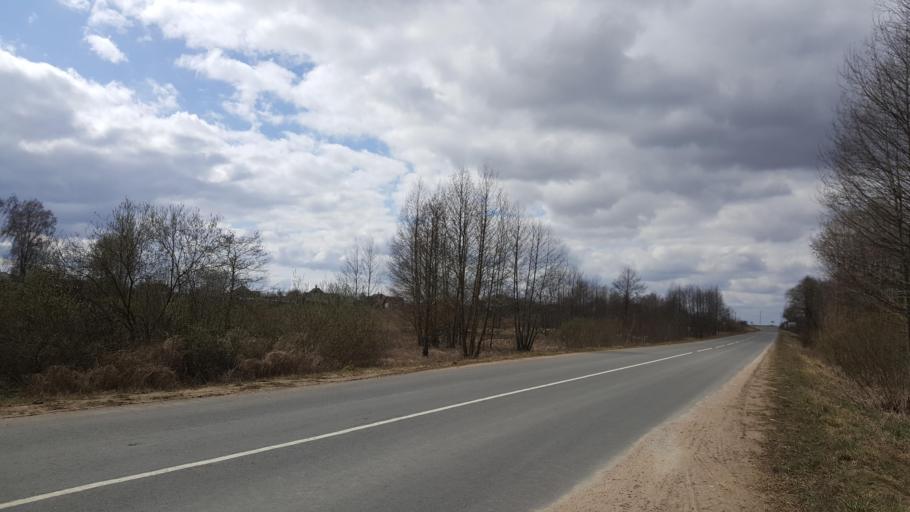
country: BY
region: Brest
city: Vysokaye
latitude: 52.3712
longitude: 23.5700
